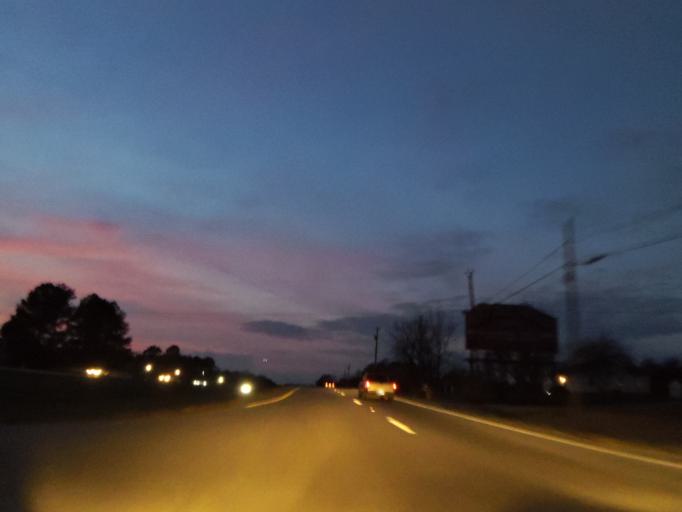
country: US
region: Tennessee
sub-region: Polk County
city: Benton
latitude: 35.1313
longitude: -84.7365
